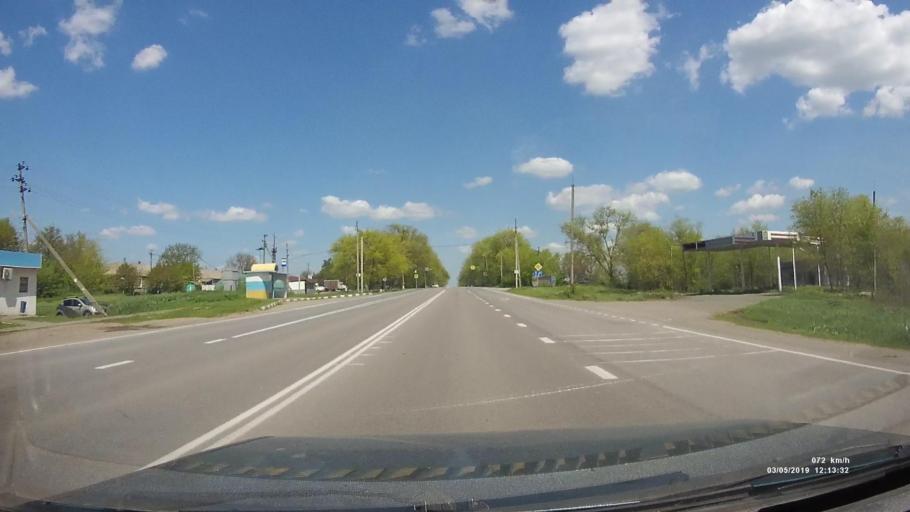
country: RU
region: Rostov
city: Melikhovskaya
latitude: 47.3337
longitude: 40.5557
